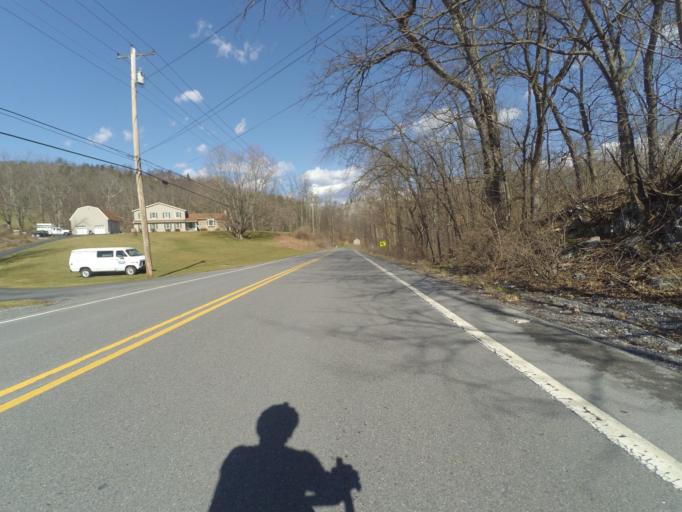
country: US
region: Pennsylvania
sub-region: Centre County
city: Park Forest Village
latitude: 40.8263
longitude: -77.9664
